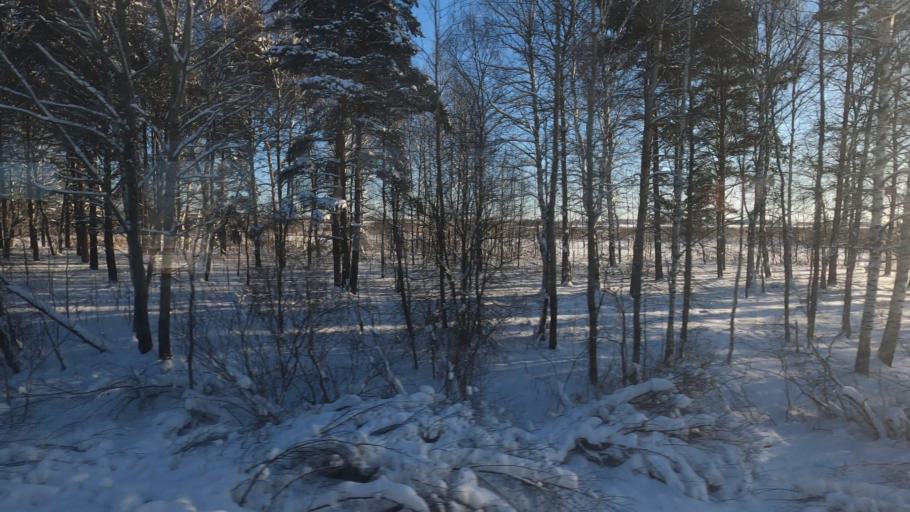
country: RU
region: Moskovskaya
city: Orud'yevo
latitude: 56.4324
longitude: 37.5016
